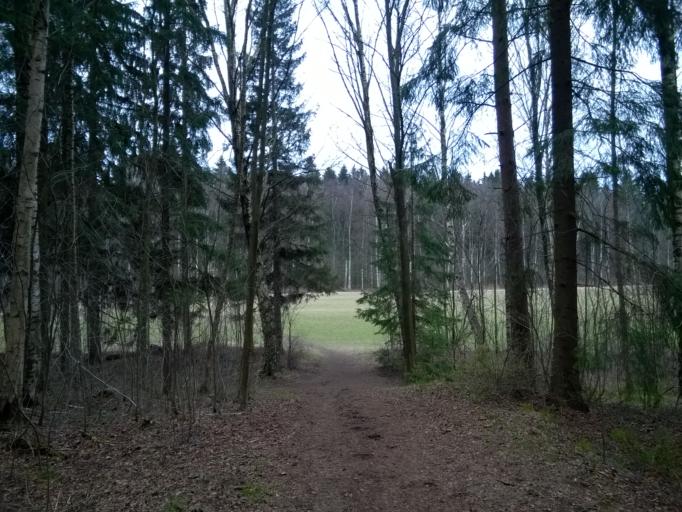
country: FI
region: Uusimaa
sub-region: Helsinki
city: Vantaa
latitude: 60.2170
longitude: 25.0313
